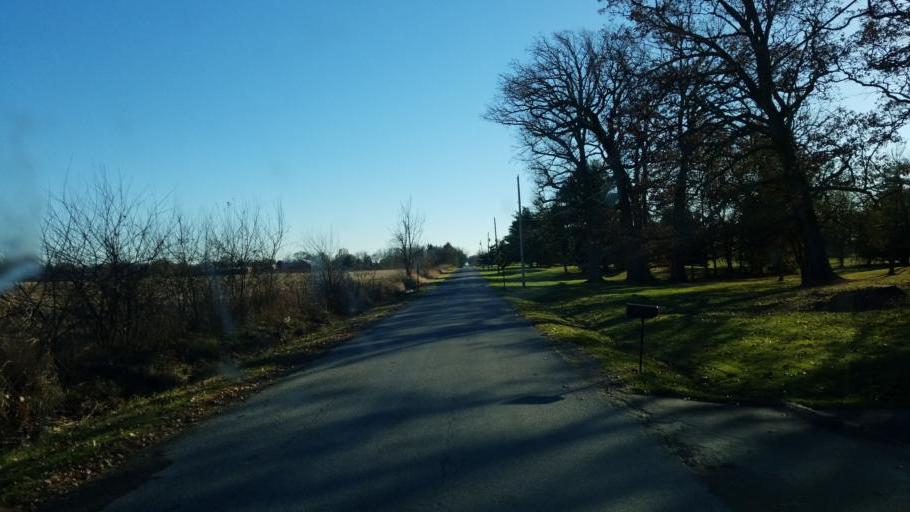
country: US
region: Ohio
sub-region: Morrow County
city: Cardington
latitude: 40.4647
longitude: -82.8951
